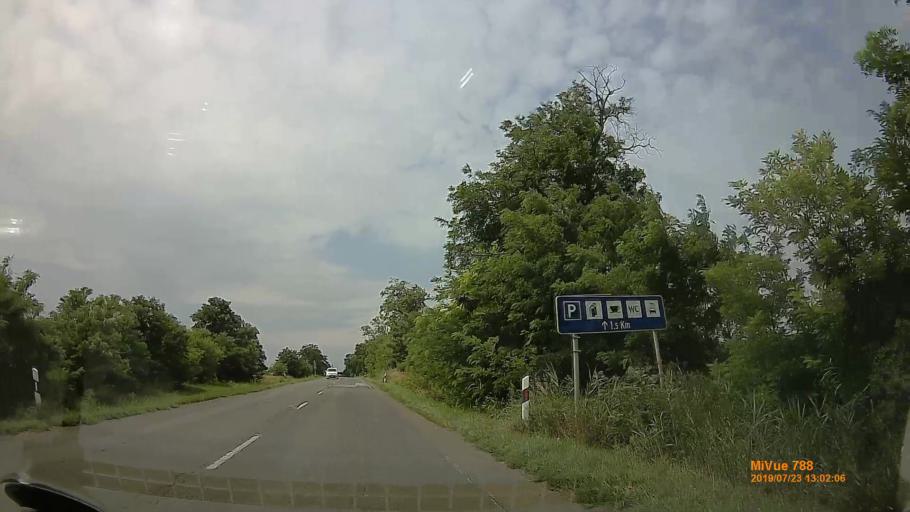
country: HU
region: Szabolcs-Szatmar-Bereg
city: Tiszavasvari
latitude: 47.9577
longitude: 21.3922
